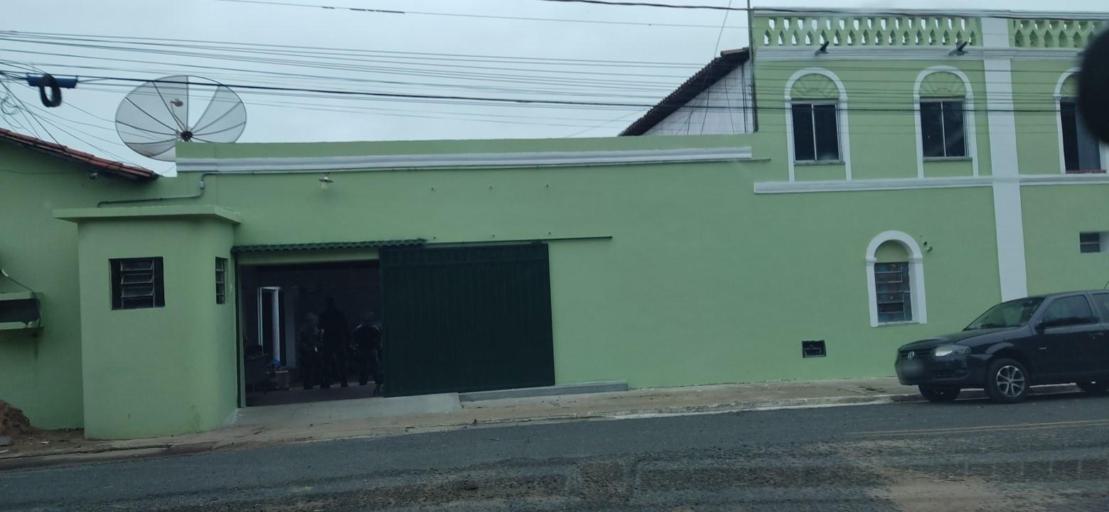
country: BR
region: Piaui
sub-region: Valenca Do Piaui
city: Valenca do Piaui
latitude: -6.4022
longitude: -41.7422
